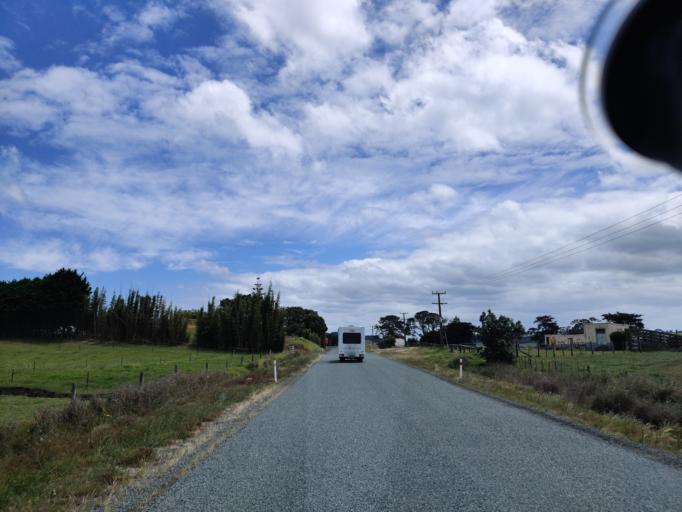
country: NZ
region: Northland
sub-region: Far North District
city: Kaitaia
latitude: -34.7744
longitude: 173.0911
